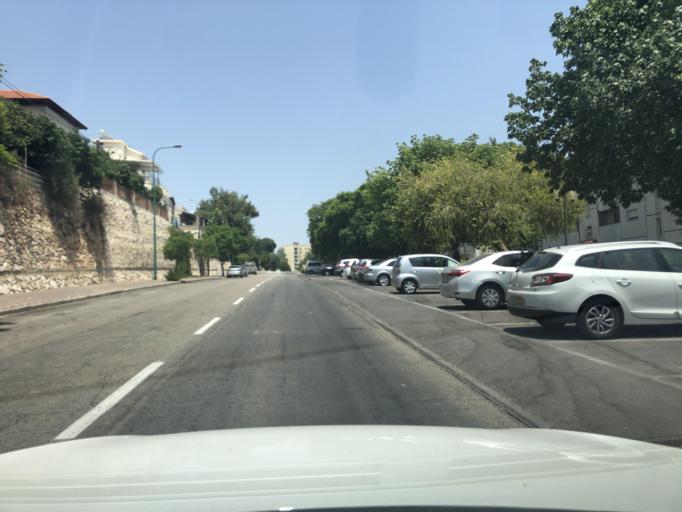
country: IL
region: Haifa
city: Daliyat el Karmil
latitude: 32.6503
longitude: 35.0959
